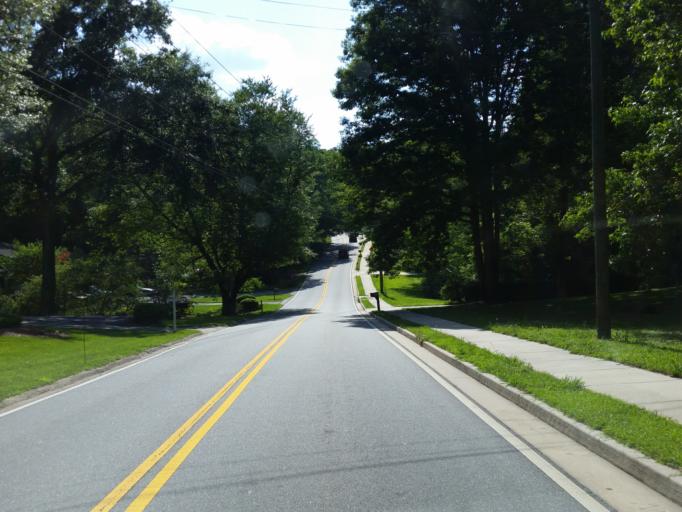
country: US
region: Georgia
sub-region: Cobb County
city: Marietta
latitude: 33.9873
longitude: -84.4888
